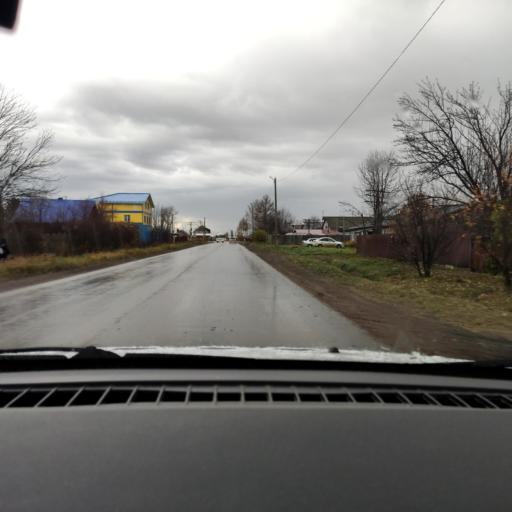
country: RU
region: Perm
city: Kultayevo
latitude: 57.8993
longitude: 55.9563
